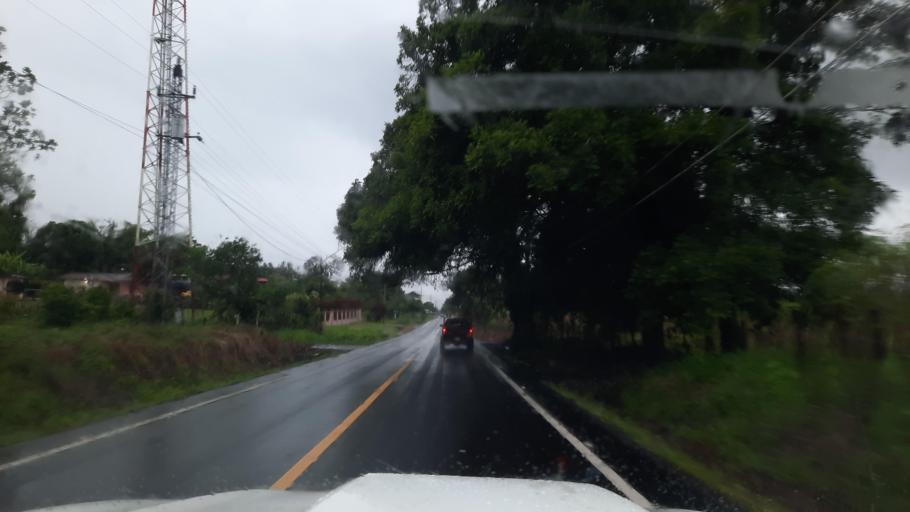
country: PA
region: Chiriqui
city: Sortova
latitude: 8.5536
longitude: -82.6265
